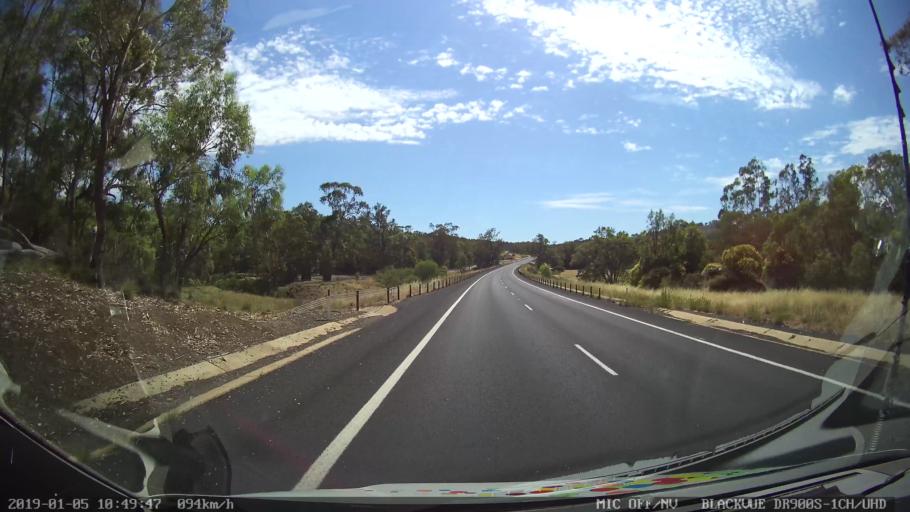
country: AU
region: New South Wales
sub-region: Warrumbungle Shire
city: Coonabarabran
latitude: -31.4317
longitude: 149.0656
